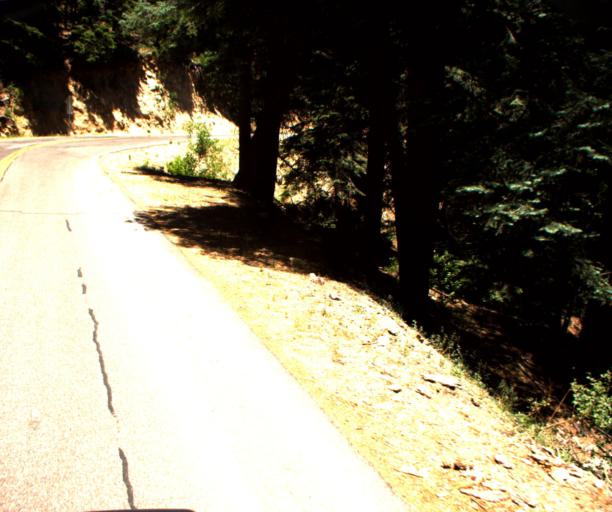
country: US
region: Arizona
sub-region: Graham County
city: Swift Trail Junction
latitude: 32.6266
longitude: -109.8273
